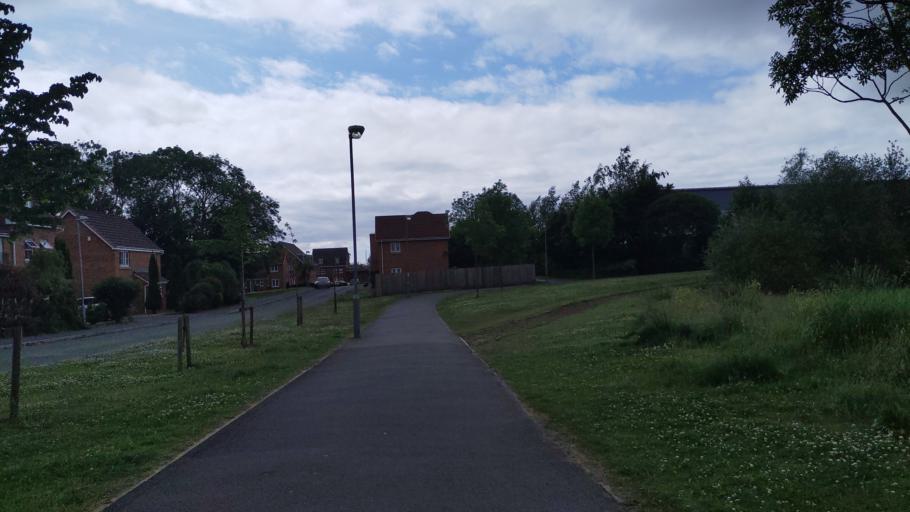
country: GB
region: England
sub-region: Lancashire
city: Clayton-le-Woods
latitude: 53.6828
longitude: -2.6685
